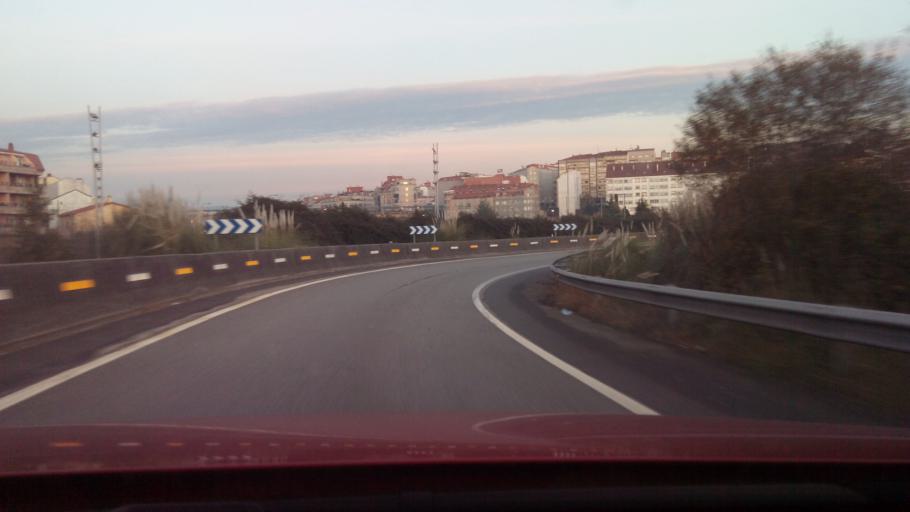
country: ES
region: Galicia
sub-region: Provincia de Pontevedra
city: Poio
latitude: 42.4318
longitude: -8.6570
